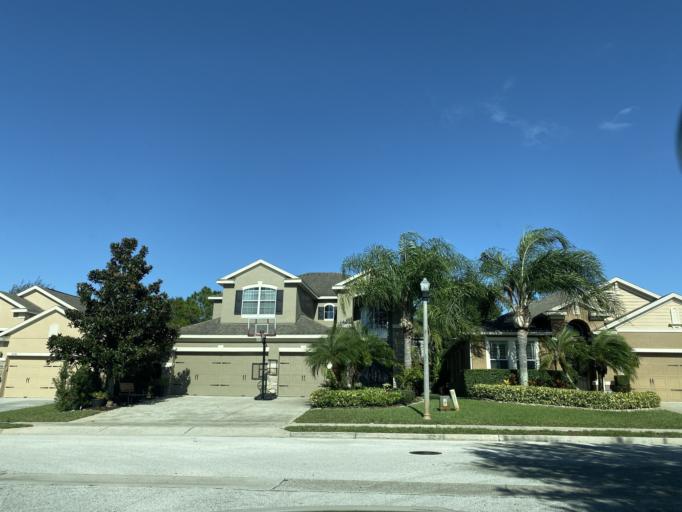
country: US
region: Florida
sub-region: Seminole County
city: Goldenrod
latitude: 28.6146
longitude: -81.2627
